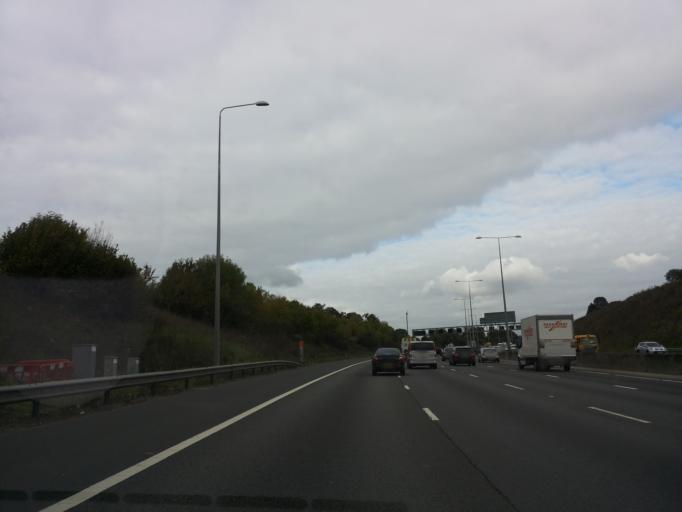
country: GB
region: England
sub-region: Hertfordshire
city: Chorleywood
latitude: 51.6660
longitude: -0.4934
